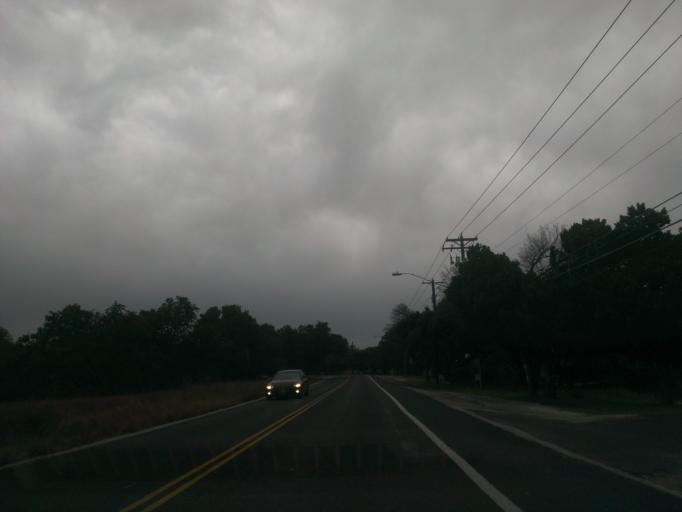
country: US
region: Texas
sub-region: Williamson County
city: Jollyville
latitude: 30.3795
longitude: -97.7652
